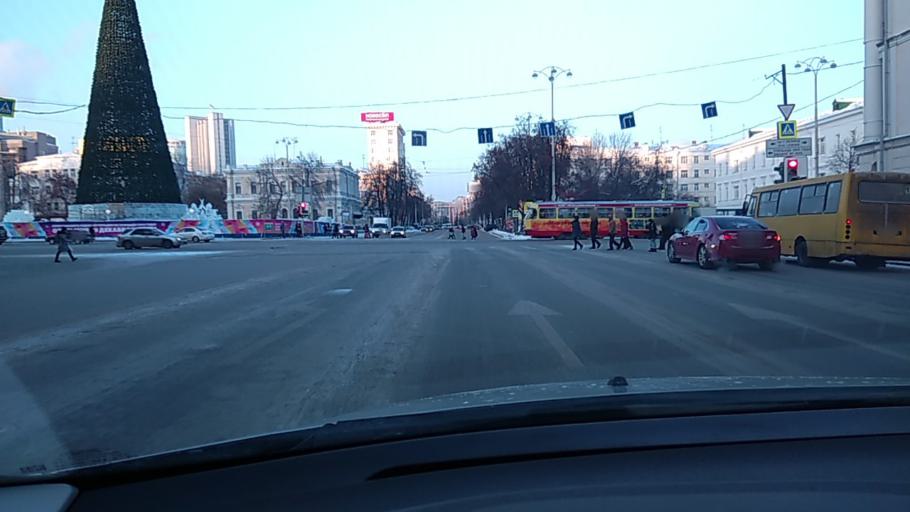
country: RU
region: Sverdlovsk
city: Yekaterinburg
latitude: 56.8373
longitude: 60.5991
